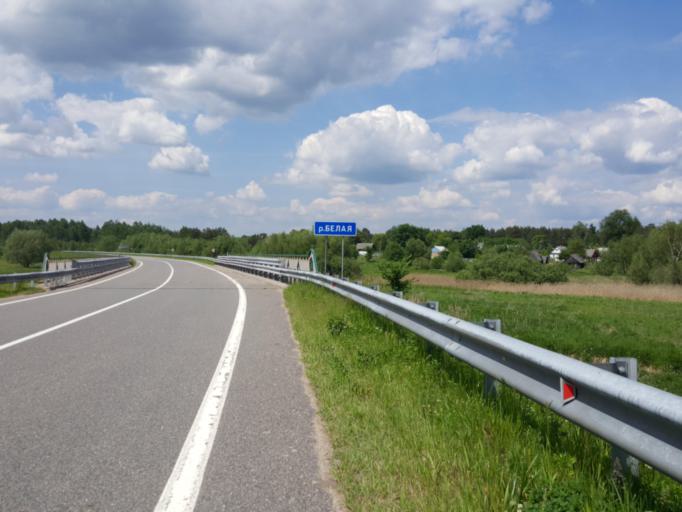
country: BY
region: Brest
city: Kamyanyuki
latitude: 52.5478
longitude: 23.6519
